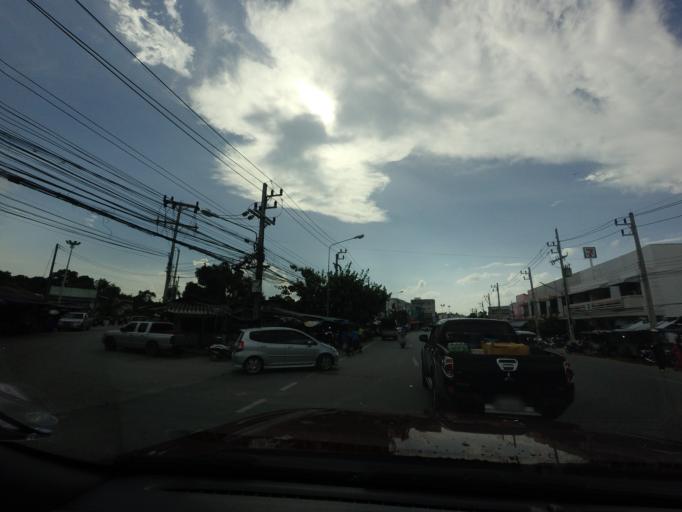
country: TH
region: Pattani
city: Khok Pho
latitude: 6.6771
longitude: 101.1474
